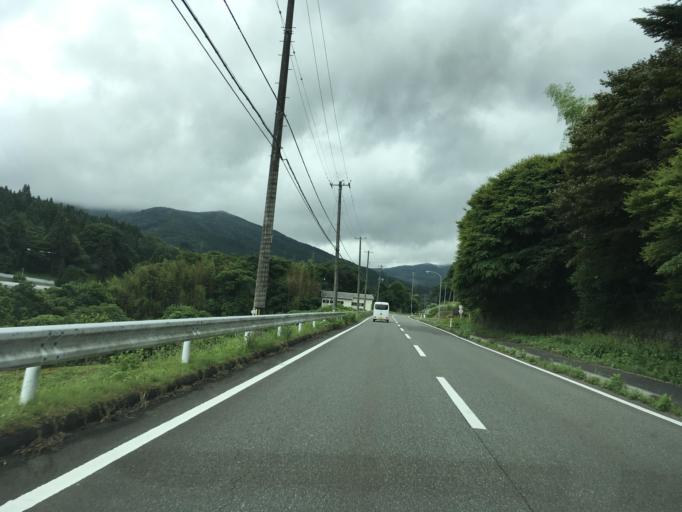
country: JP
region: Iwate
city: Ofunato
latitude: 38.8973
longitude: 141.4877
